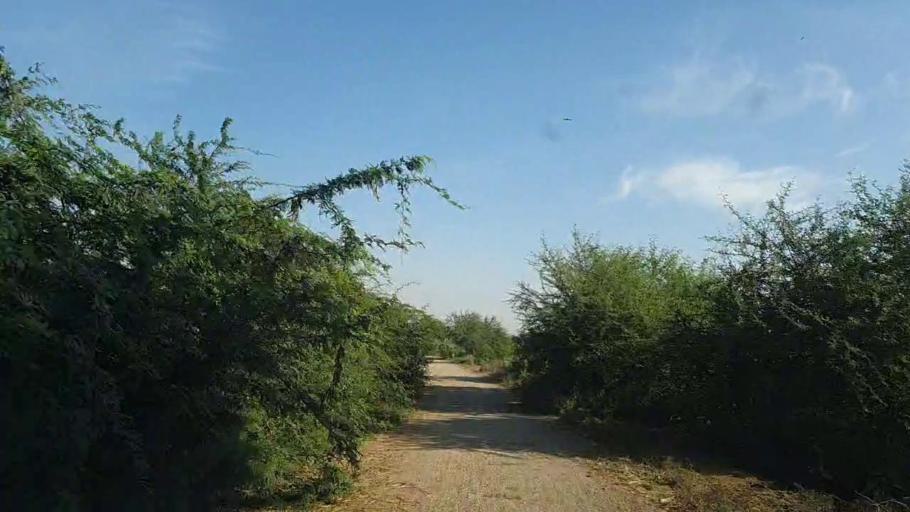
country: PK
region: Sindh
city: Bulri
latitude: 24.7785
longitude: 68.3560
